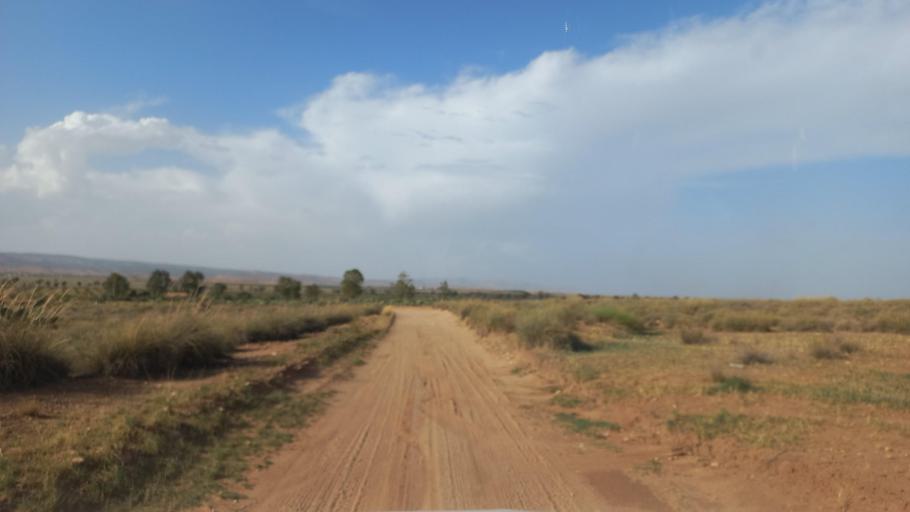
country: TN
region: Al Qasrayn
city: Kasserine
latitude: 35.2223
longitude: 8.9695
